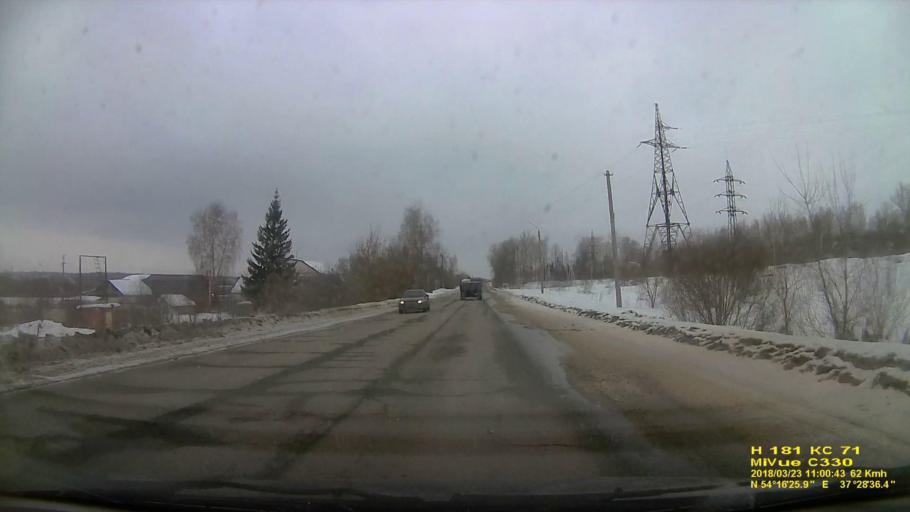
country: RU
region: Tula
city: Barsuki
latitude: 54.2740
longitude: 37.4766
